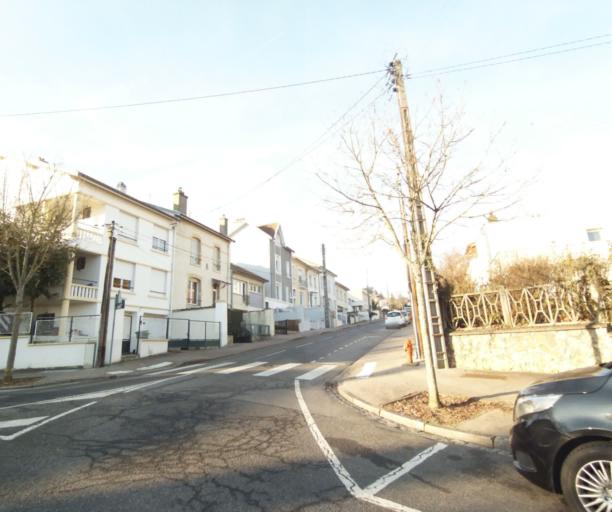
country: FR
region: Lorraine
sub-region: Departement de Meurthe-et-Moselle
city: Laxou
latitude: 48.6952
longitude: 6.1493
